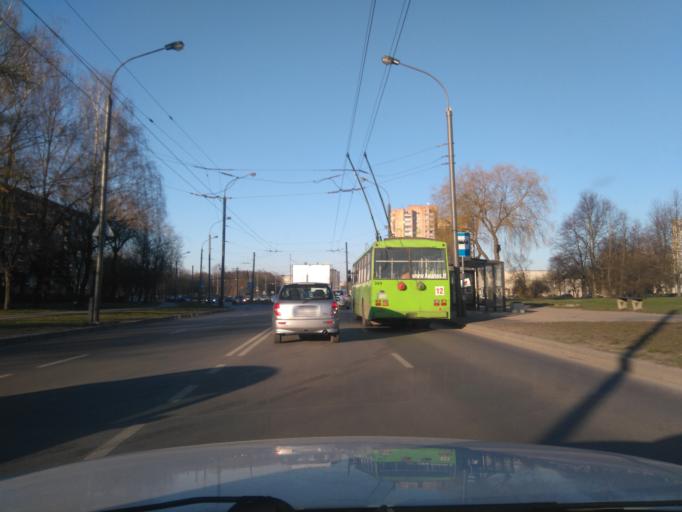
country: LT
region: Kauno apskritis
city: Dainava (Kaunas)
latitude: 54.9198
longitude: 23.9725
